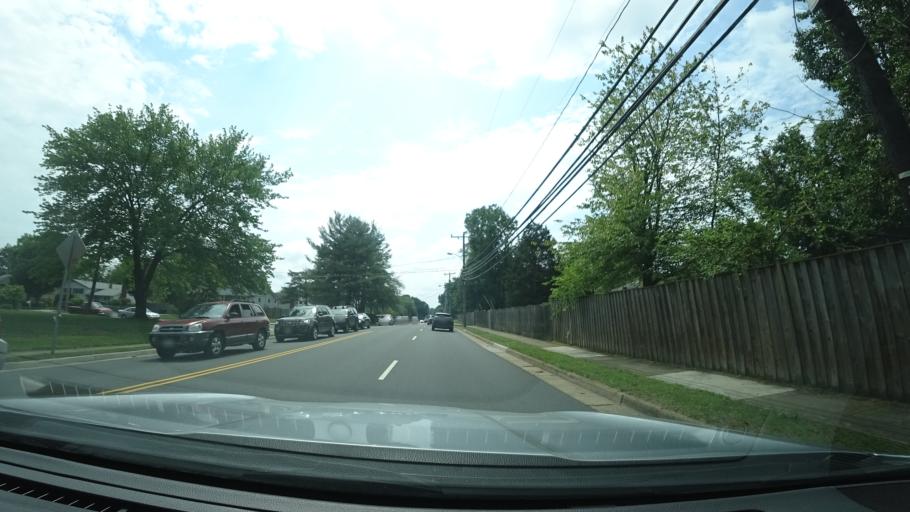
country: US
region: Virginia
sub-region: Loudoun County
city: Oak Grove
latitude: 38.9748
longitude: -77.4034
